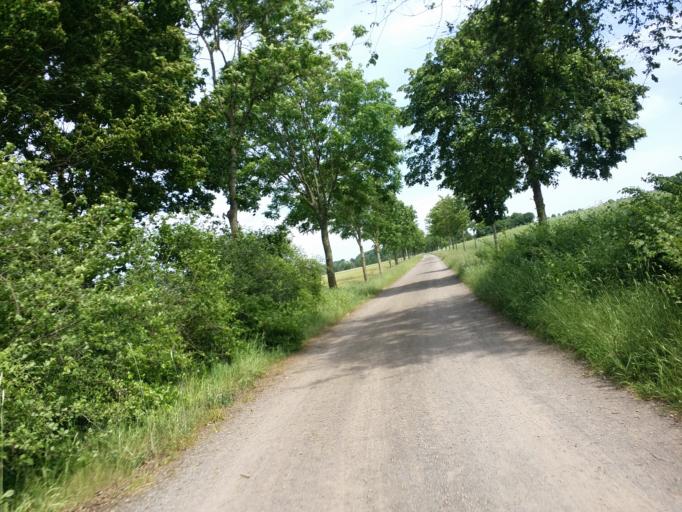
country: DE
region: Lower Saxony
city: Syke
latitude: 52.9721
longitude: 8.8631
